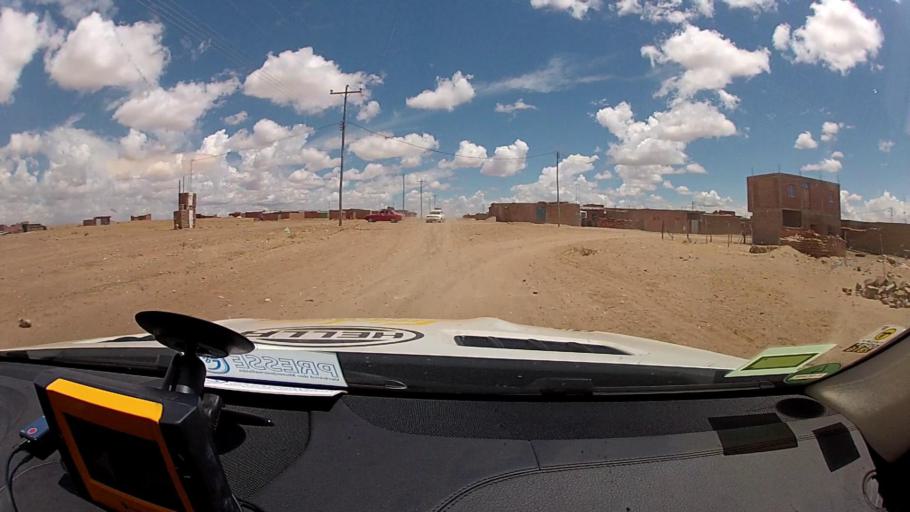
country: BO
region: Potosi
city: Villazon
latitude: -22.0807
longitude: -65.6101
